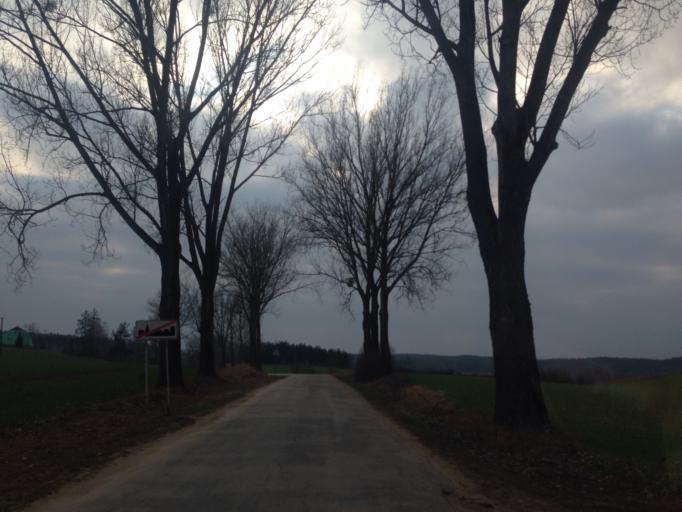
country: PL
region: Warmian-Masurian Voivodeship
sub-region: Powiat dzialdowski
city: Lidzbark
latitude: 53.3522
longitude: 19.7577
